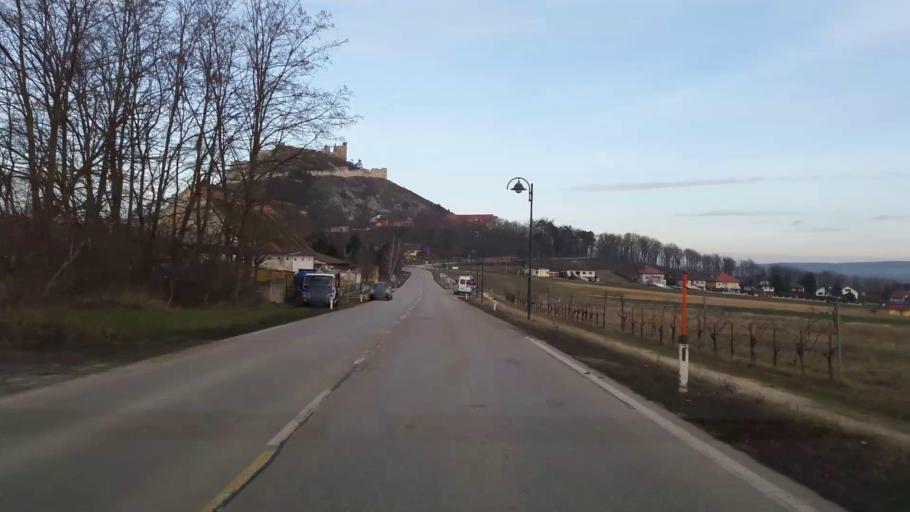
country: AT
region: Lower Austria
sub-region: Politischer Bezirk Mistelbach
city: Staatz
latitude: 48.6712
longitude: 16.4914
